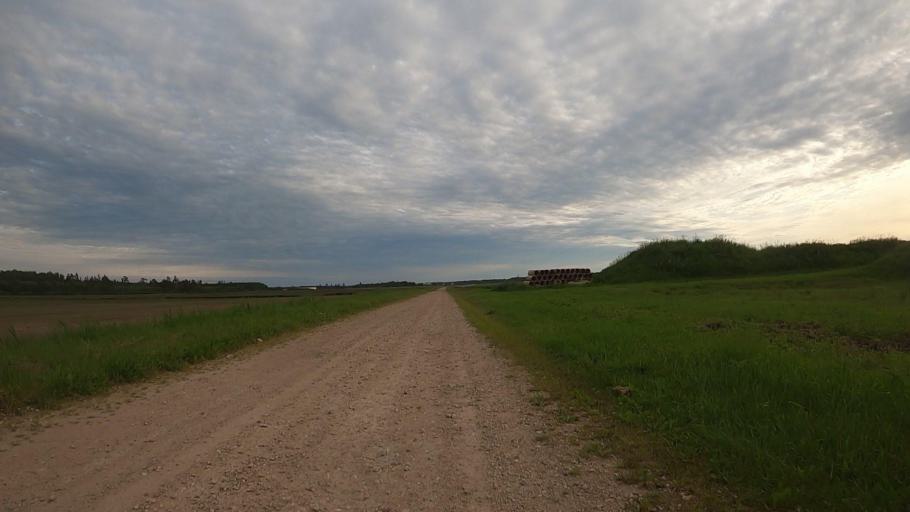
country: LV
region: Olaine
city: Olaine
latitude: 56.8241
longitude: 23.9559
